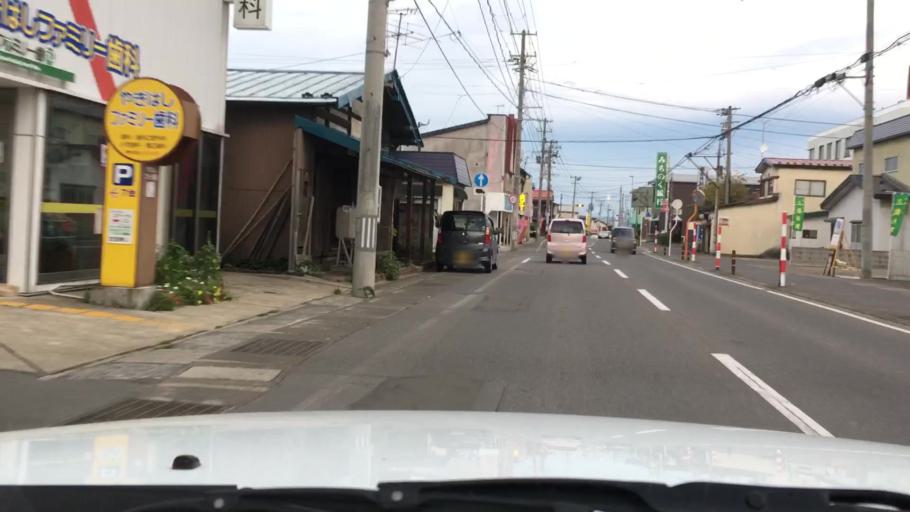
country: JP
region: Aomori
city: Hirosaki
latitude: 40.5892
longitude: 140.4820
